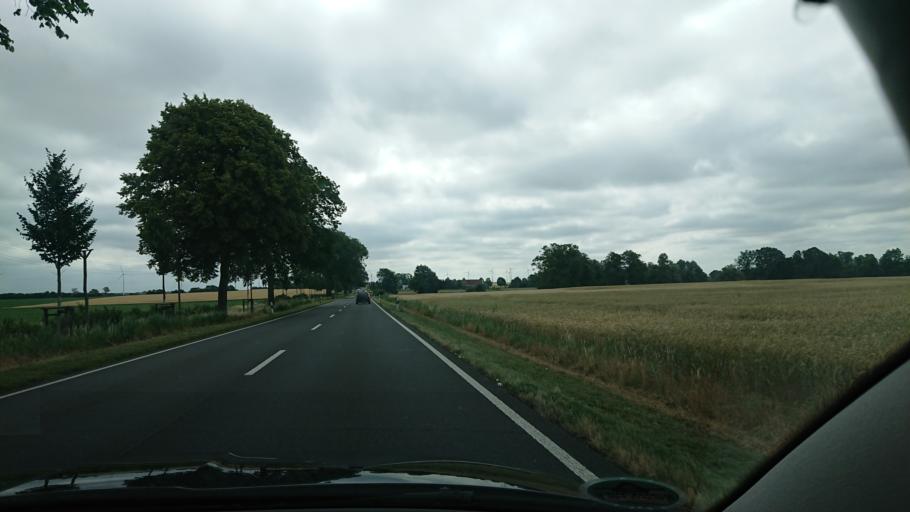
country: DE
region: Brandenburg
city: Plattenburg
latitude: 53.0034
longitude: 12.0550
